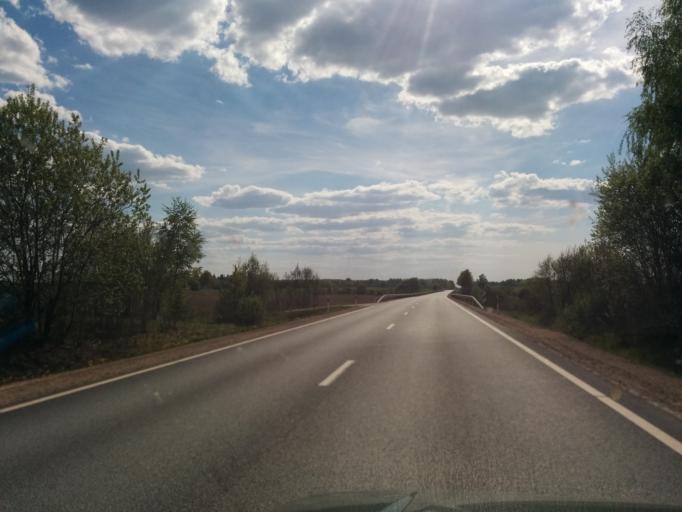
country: LV
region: Sigulda
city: Sigulda
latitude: 57.2433
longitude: 24.8384
